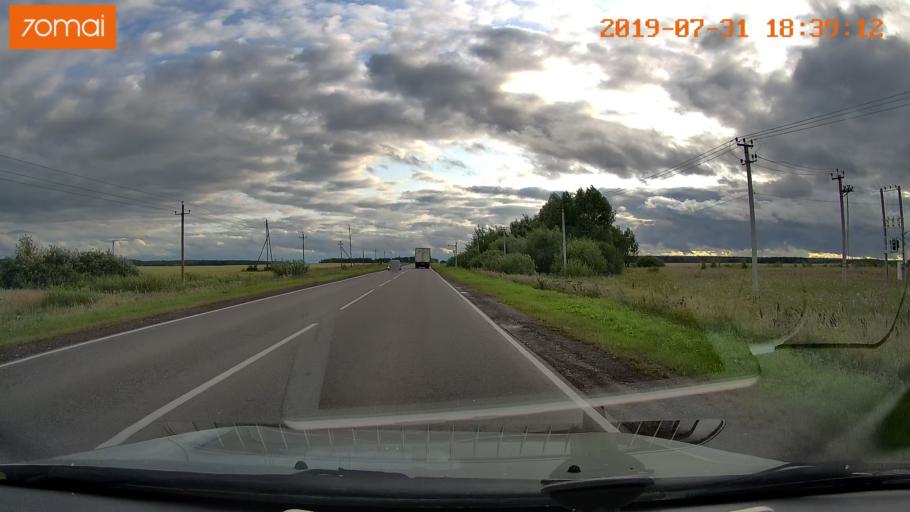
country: RU
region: Moskovskaya
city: Voskresensk
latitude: 55.2689
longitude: 38.6484
